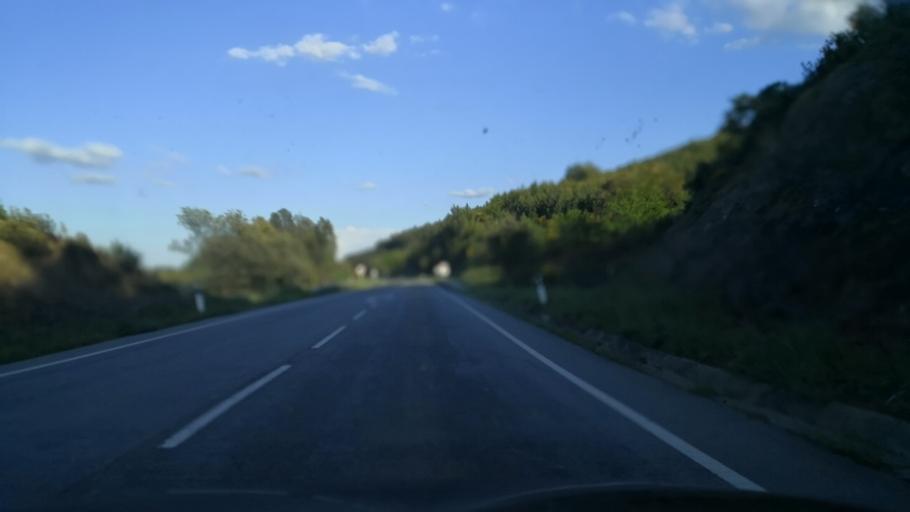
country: PT
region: Portalegre
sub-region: Marvao
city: Marvao
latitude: 39.3763
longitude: -7.3636
